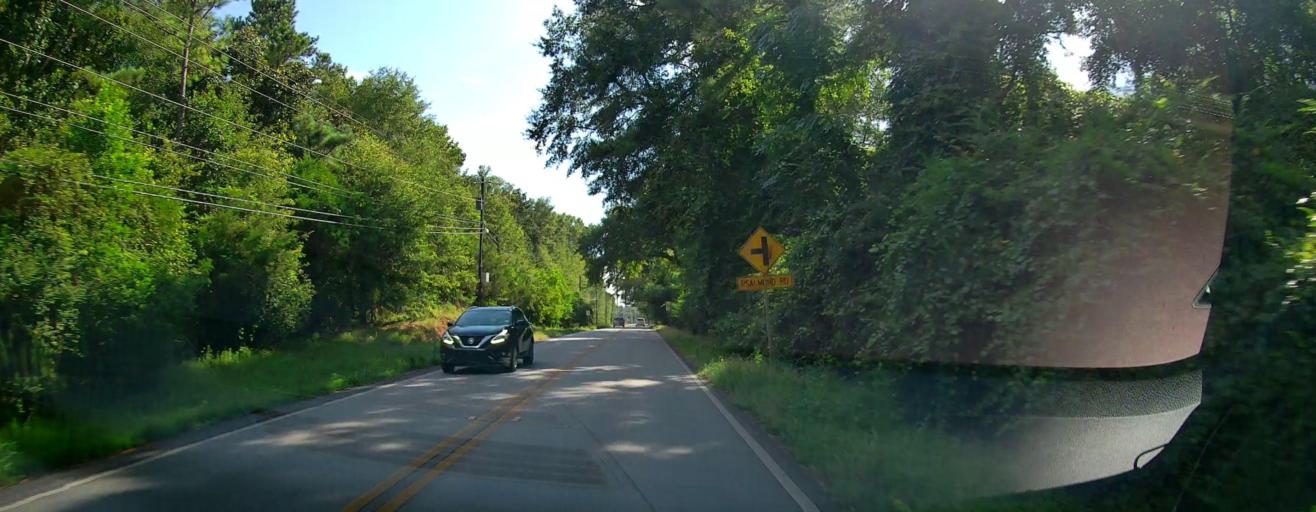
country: US
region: Georgia
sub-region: Muscogee County
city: Columbus
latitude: 32.5591
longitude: -84.8636
